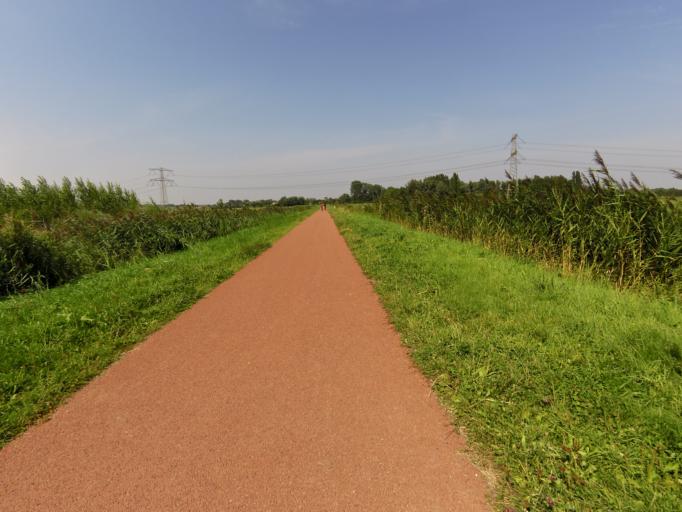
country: NL
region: South Holland
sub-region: Gemeente Dordrecht
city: Dordrecht
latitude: 51.7658
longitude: 4.6823
